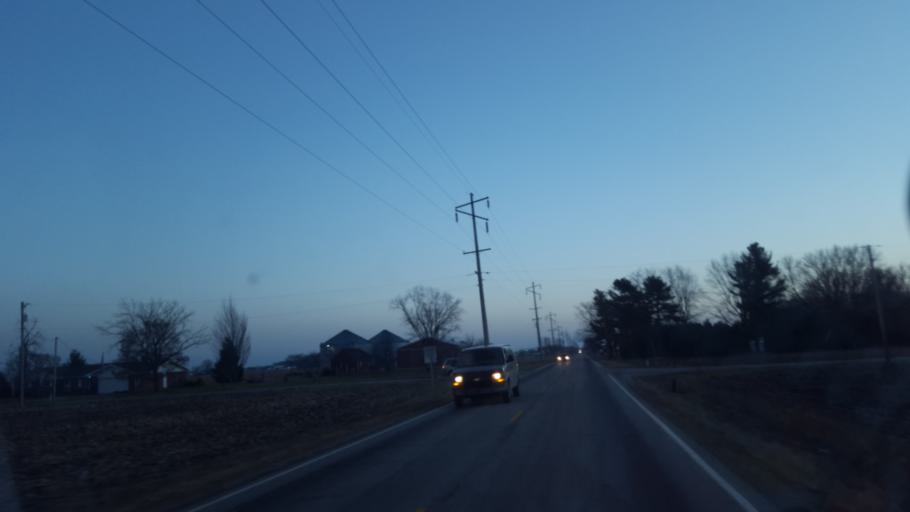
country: US
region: Indiana
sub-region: Elkhart County
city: Nappanee
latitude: 41.3911
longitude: -86.0009
